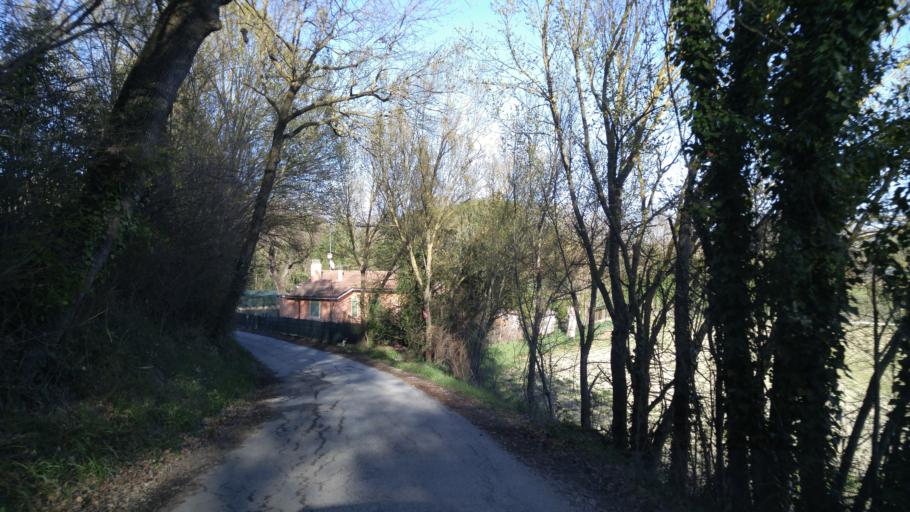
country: IT
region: The Marches
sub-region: Provincia di Pesaro e Urbino
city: Fenile
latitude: 43.8317
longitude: 12.9122
